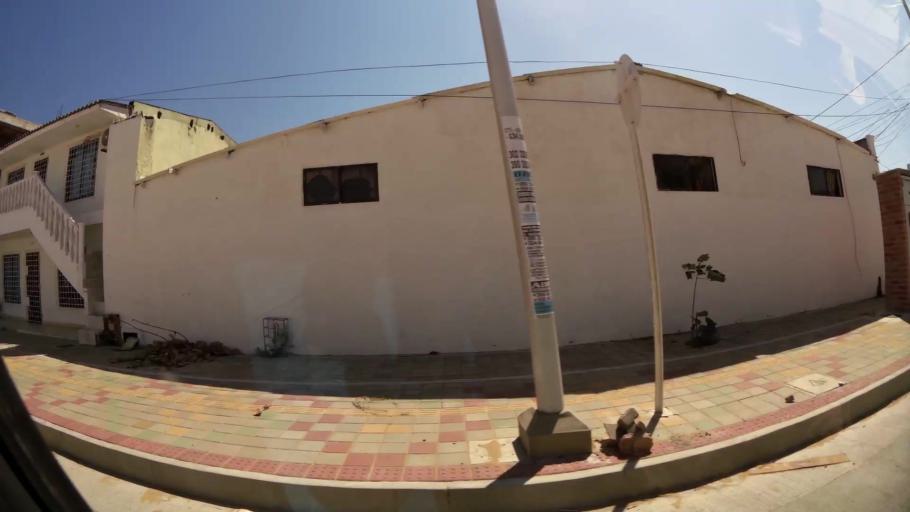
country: CO
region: Atlantico
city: Barranquilla
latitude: 11.0179
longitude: -74.8081
